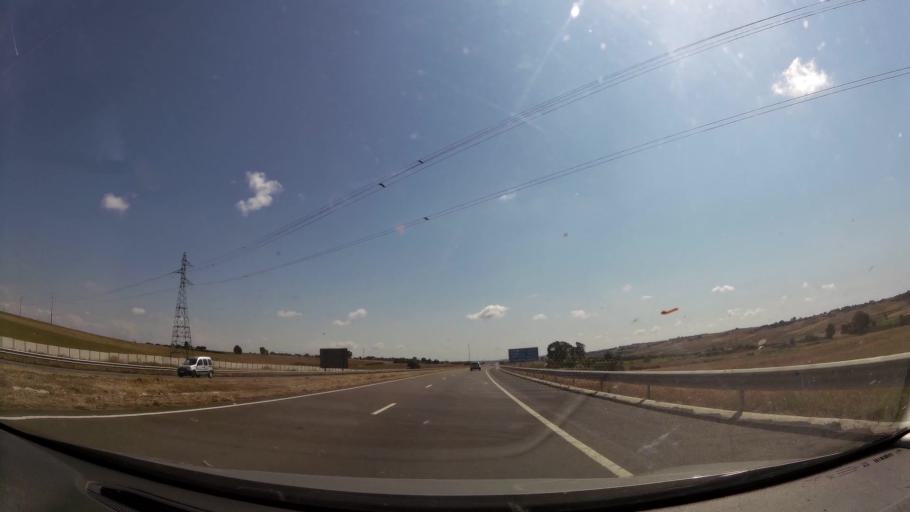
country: MA
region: Rabat-Sale-Zemmour-Zaer
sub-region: Rabat
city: Rabat
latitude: 33.9584
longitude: -6.7466
